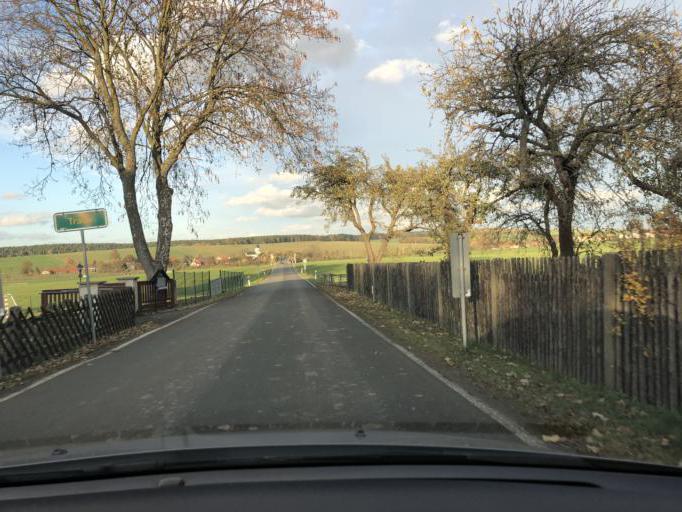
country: DE
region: Thuringia
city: Miesitz
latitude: 50.7348
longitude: 11.8201
